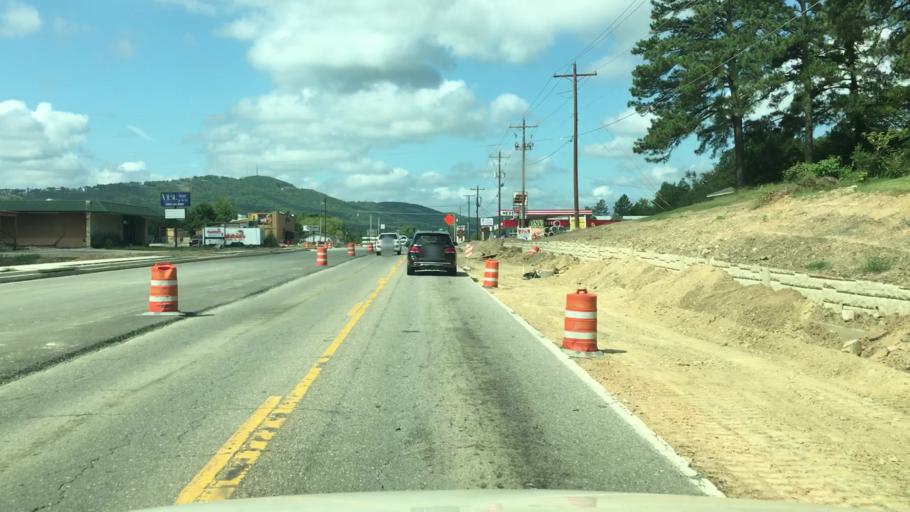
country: US
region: Arkansas
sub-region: Garland County
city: Lake Hamilton
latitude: 34.4259
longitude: -93.0928
